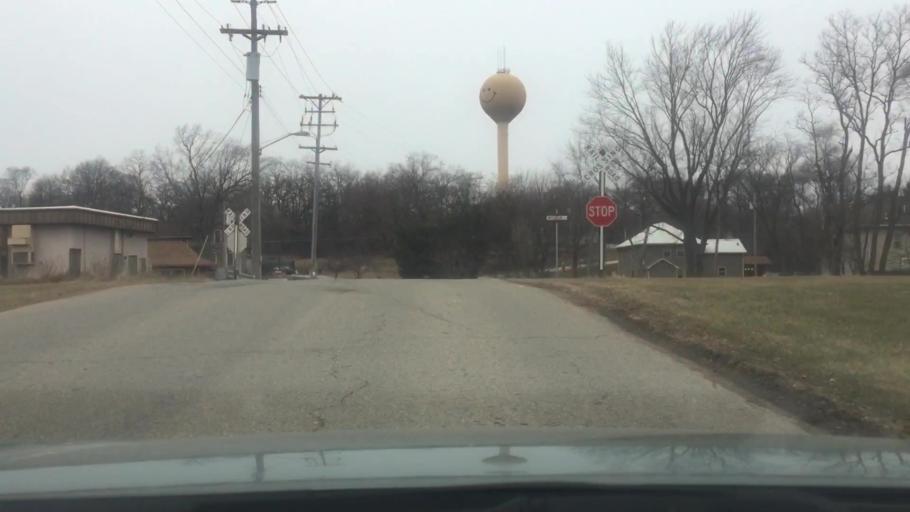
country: US
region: Wisconsin
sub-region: Waukesha County
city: Eagle
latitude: 42.8800
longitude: -88.4726
